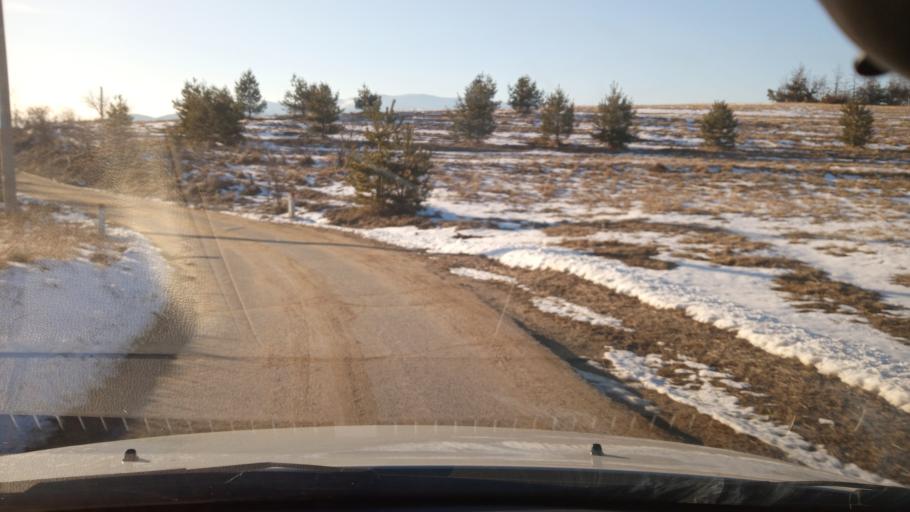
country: BG
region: Sofiya
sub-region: Obshtina Samokov
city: Samokov
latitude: 42.4789
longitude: 23.4199
